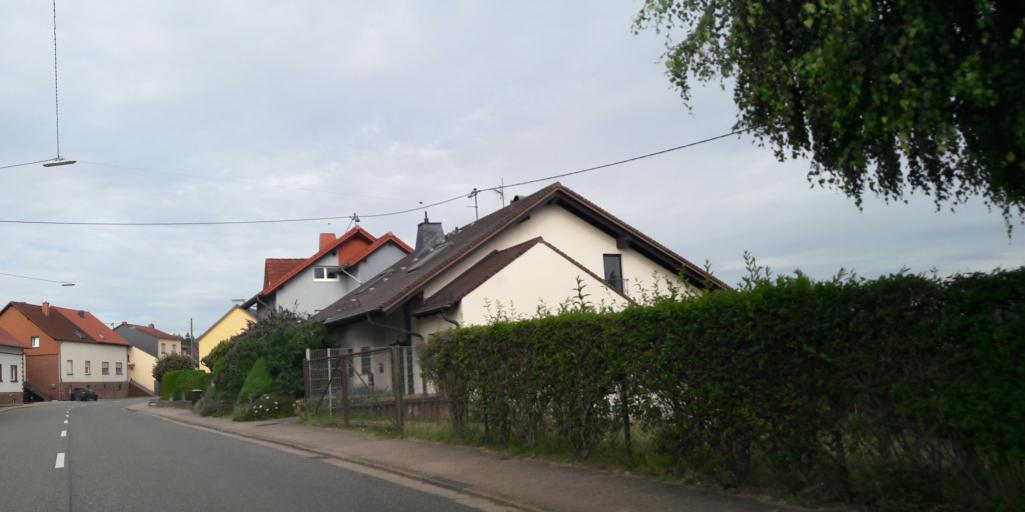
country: DE
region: Saarland
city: Puttlingen
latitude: 49.3025
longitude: 6.8891
